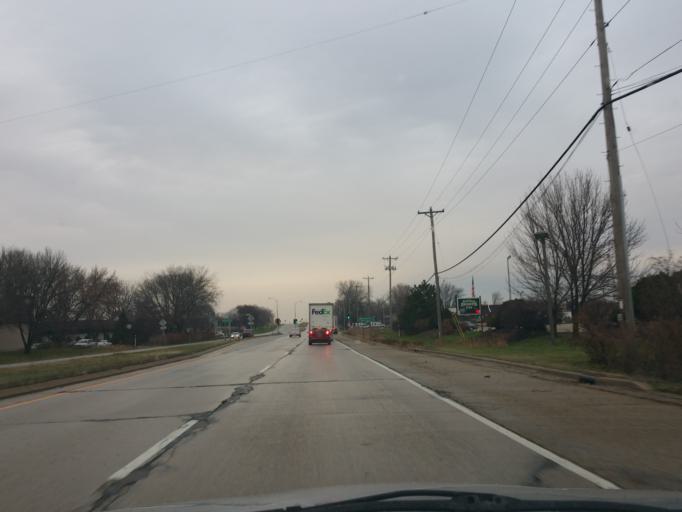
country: US
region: Wisconsin
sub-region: Dane County
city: Maple Bluff
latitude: 43.1238
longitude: -89.3249
